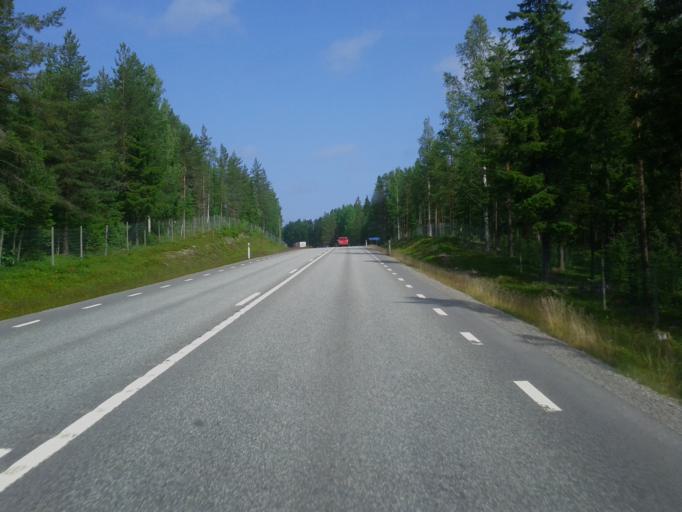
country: SE
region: Vaesterbotten
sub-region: Skelleftea Kommun
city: Burea
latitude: 64.5330
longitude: 21.2588
